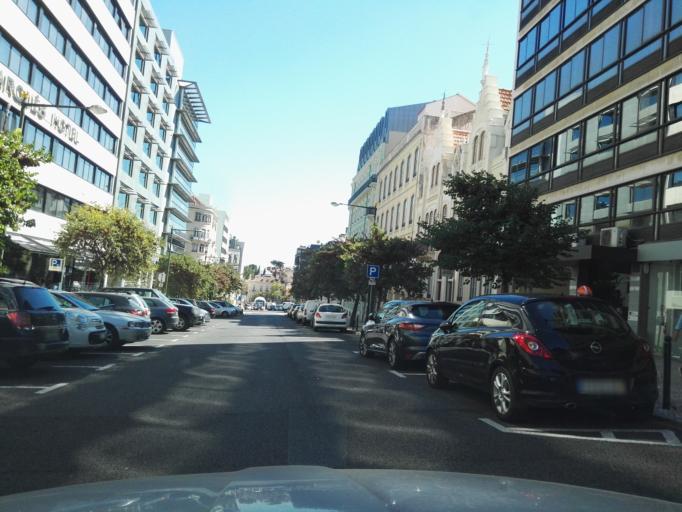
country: PT
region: Lisbon
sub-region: Lisbon
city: Lisbon
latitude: 38.7232
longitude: -9.1508
